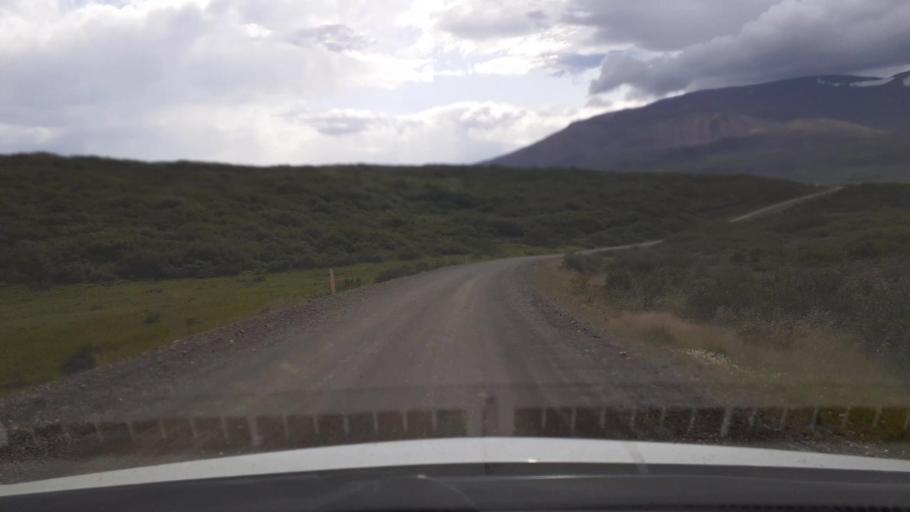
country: IS
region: West
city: Borgarnes
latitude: 64.5578
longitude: -21.6248
